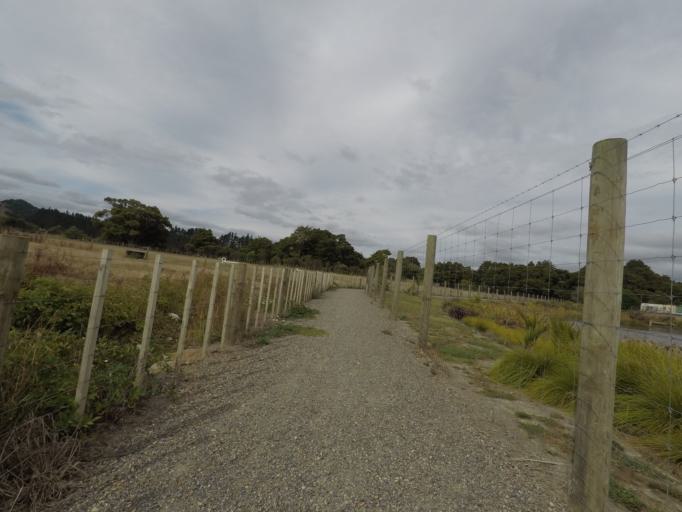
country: NZ
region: Northland
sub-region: Whangarei
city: Whangarei
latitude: -35.6782
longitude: 174.3323
